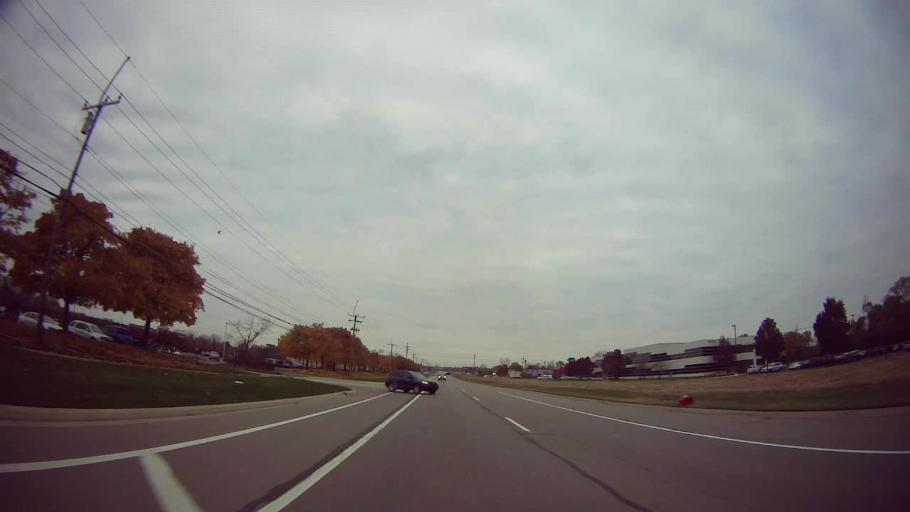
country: US
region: Michigan
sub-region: Oakland County
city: Franklin
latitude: 42.5235
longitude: -83.3481
